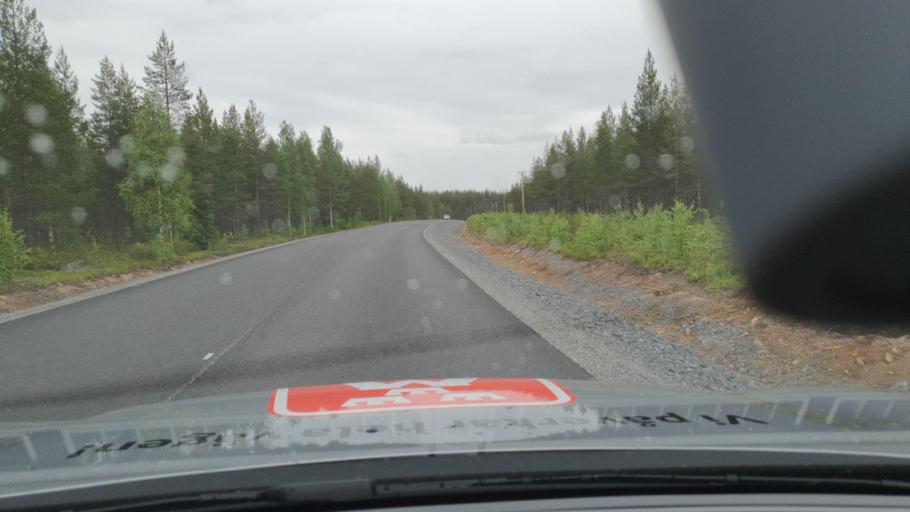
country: SE
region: Norrbotten
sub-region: Overkalix Kommun
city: OEverkalix
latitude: 66.6735
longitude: 23.2205
